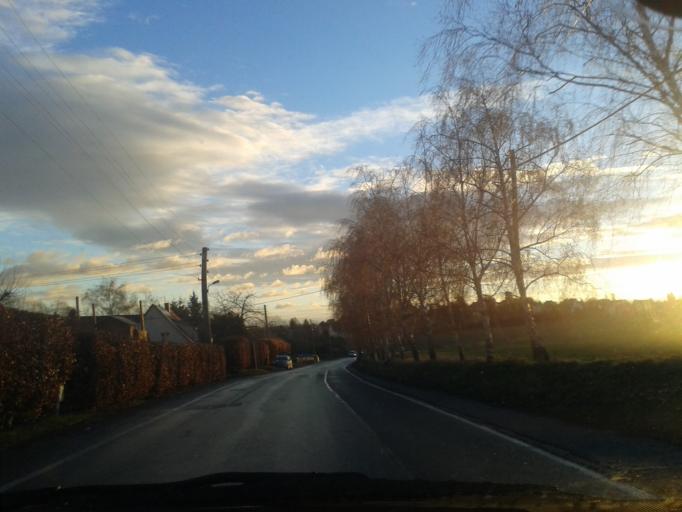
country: DE
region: Saxony
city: Bannewitz
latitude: 51.0134
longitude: 13.7377
